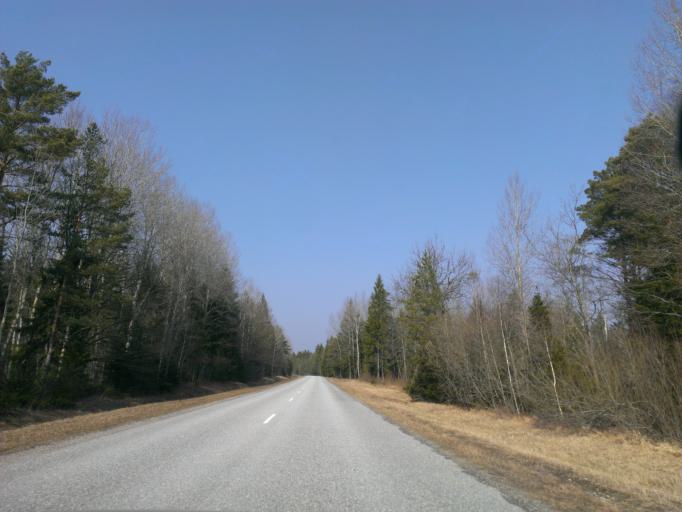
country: EE
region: Saare
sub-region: Kuressaare linn
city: Kuressaare
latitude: 58.3562
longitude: 22.6740
